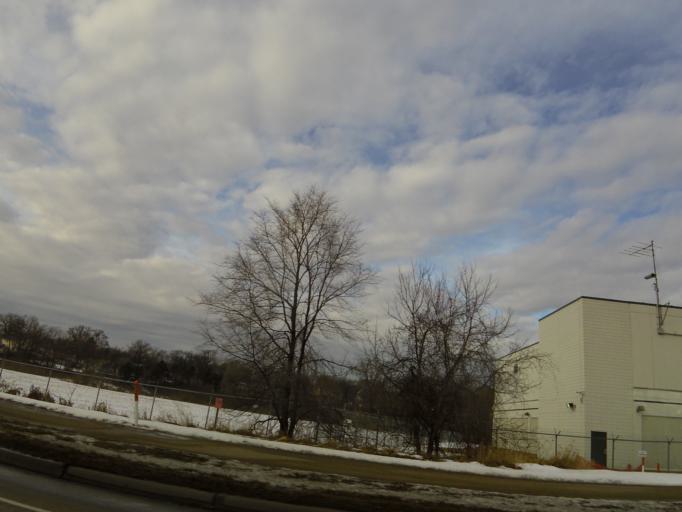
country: US
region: Minnesota
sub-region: Ramsey County
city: Saint Paul
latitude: 44.9668
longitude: -93.0571
